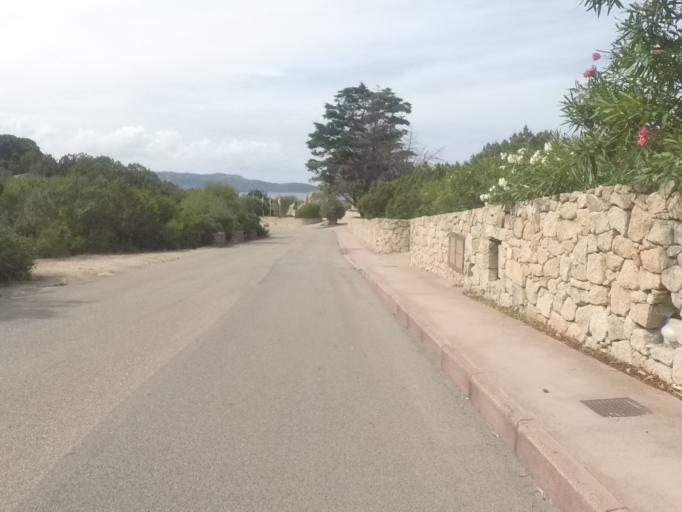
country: IT
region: Sardinia
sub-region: Provincia di Olbia-Tempio
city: Porto Cervo
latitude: 41.1390
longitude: 9.4697
